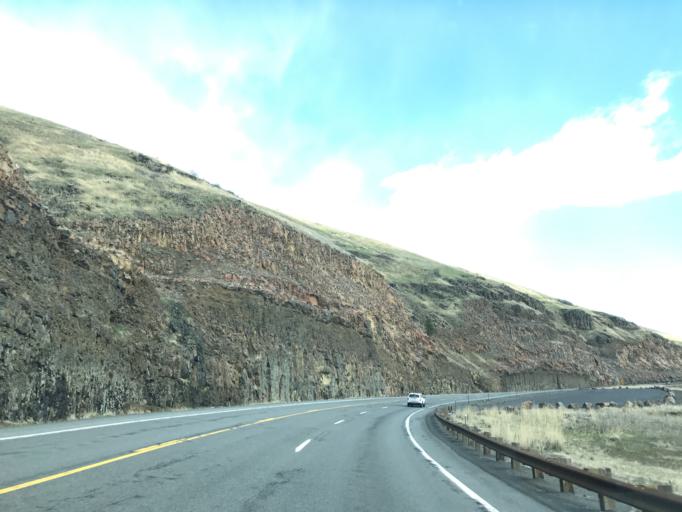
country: US
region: Idaho
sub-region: Idaho County
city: Grangeville
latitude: 45.8176
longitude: -116.2745
